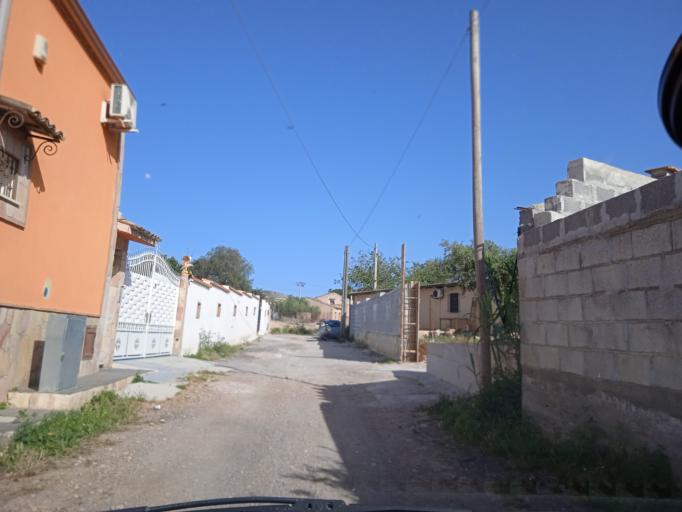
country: IT
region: Sicily
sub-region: Palermo
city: Villabate
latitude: 38.0813
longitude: 13.4531
